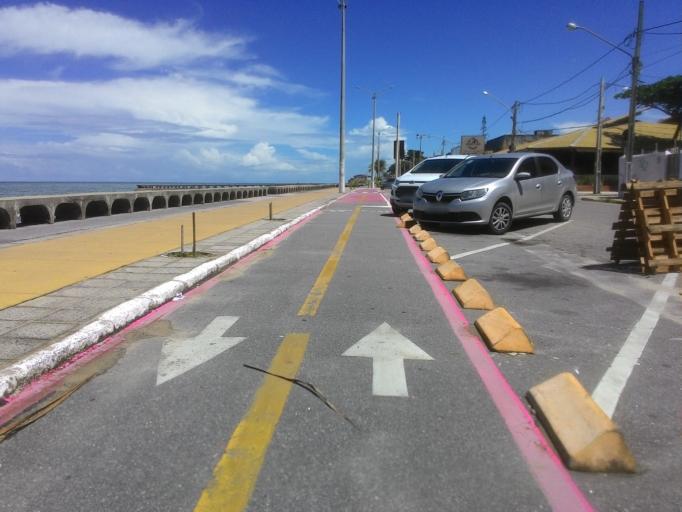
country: BR
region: Pernambuco
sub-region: Olinda
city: Olinda
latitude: -8.0079
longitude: -34.8410
